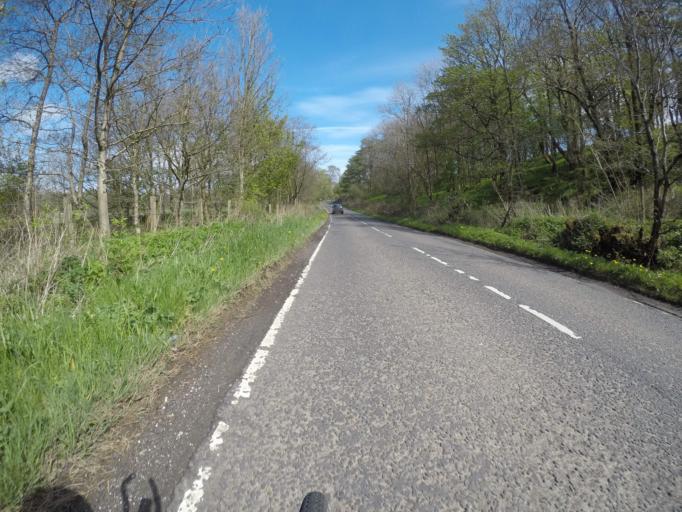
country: GB
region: Scotland
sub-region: East Ayrshire
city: Stewarton
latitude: 55.6739
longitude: -4.5241
